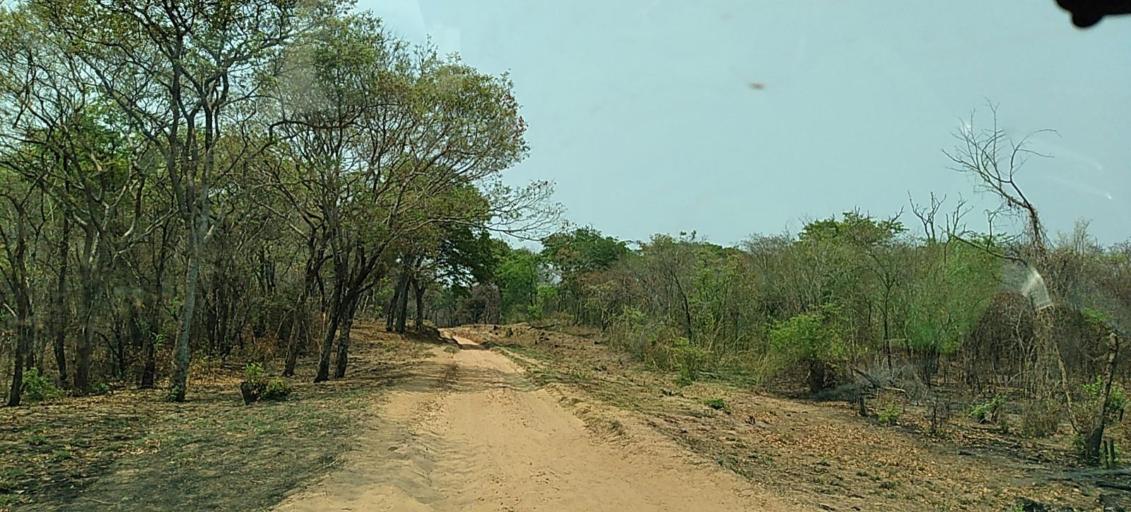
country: ZM
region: Western
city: Lukulu
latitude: -13.9835
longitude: 23.2281
